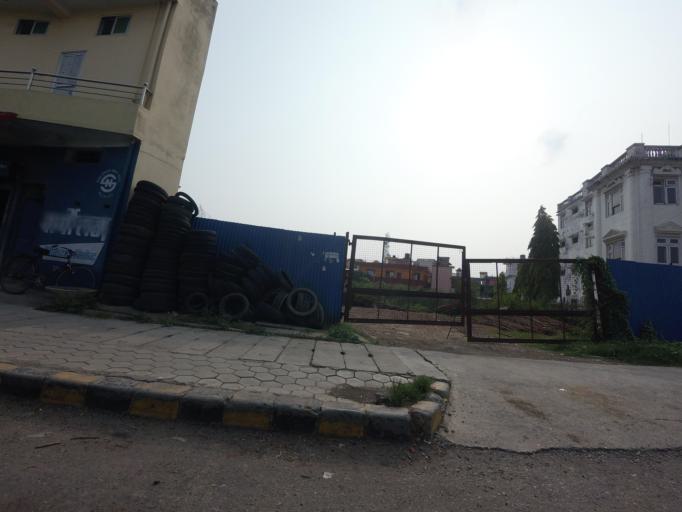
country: NP
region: Western Region
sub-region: Lumbini Zone
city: Bhairahawa
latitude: 27.5095
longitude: 83.4549
